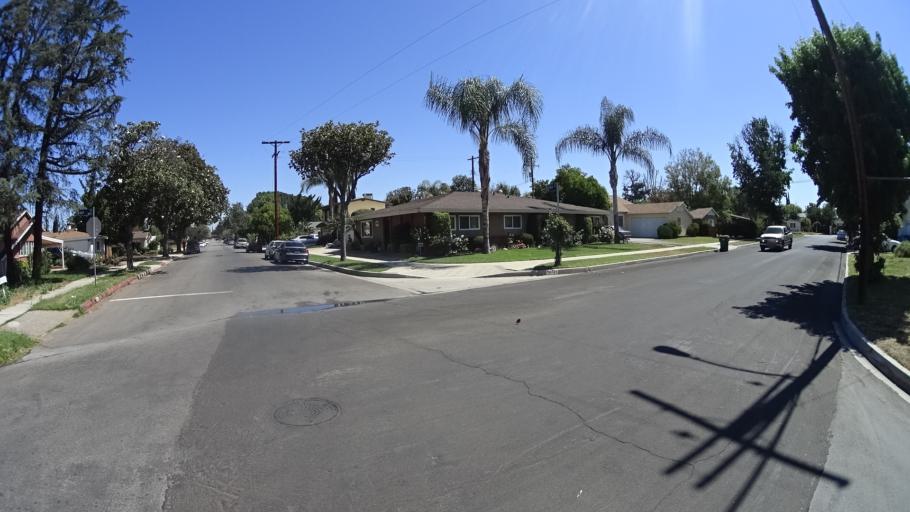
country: US
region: California
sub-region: Los Angeles County
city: Northridge
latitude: 34.1975
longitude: -118.4979
